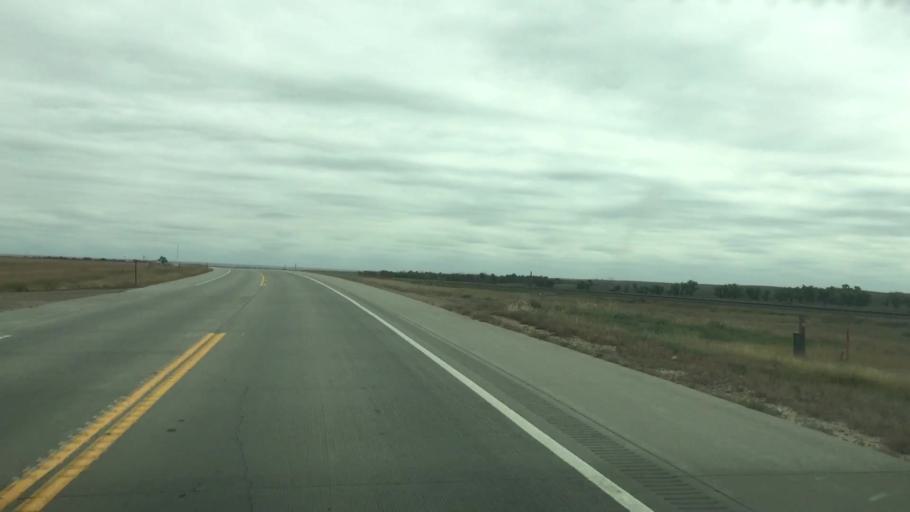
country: US
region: Colorado
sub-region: Kiowa County
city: Eads
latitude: 38.7663
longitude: -102.8500
